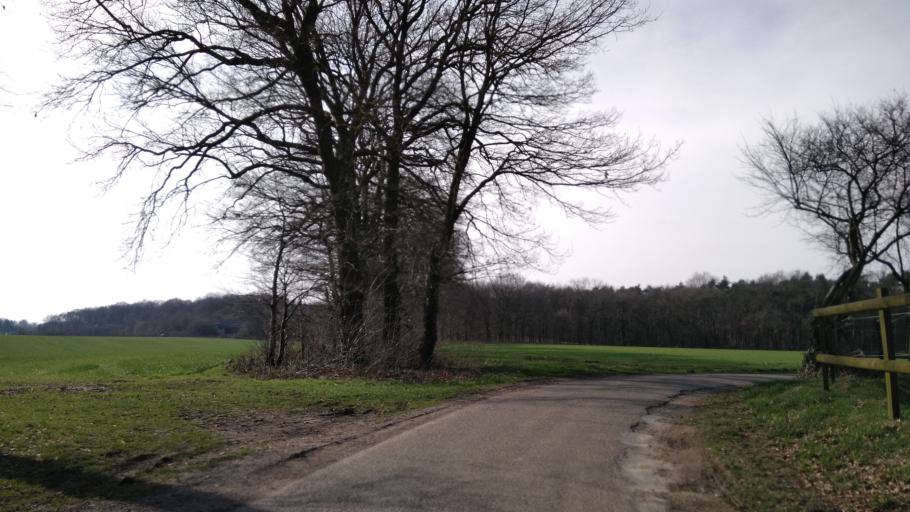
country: DE
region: North Rhine-Westphalia
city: Marl
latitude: 51.6825
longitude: 7.0289
